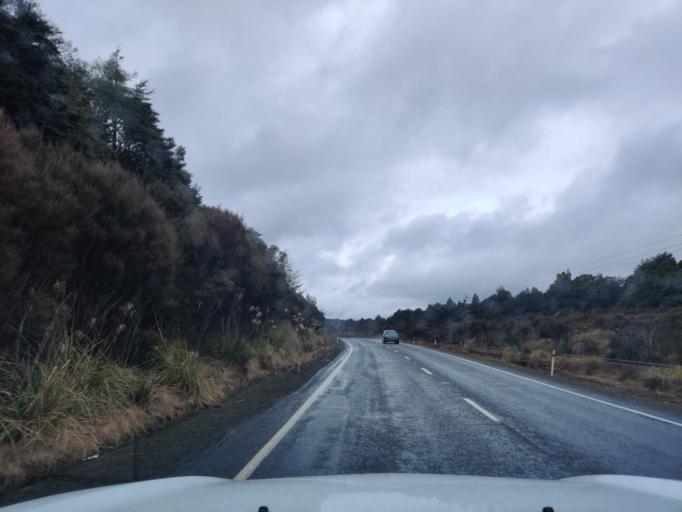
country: NZ
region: Manawatu-Wanganui
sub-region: Ruapehu District
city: Waiouru
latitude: -39.3089
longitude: 175.3895
